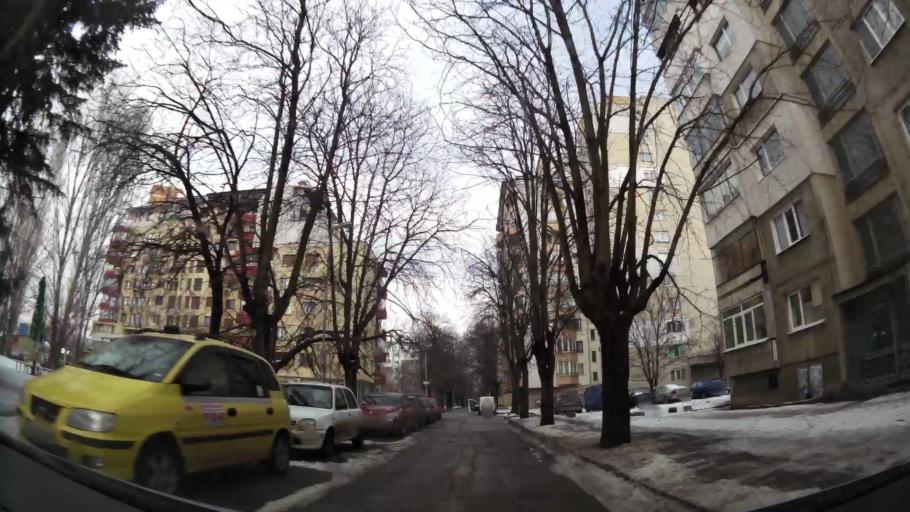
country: BG
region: Sofia-Capital
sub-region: Stolichna Obshtina
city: Sofia
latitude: 42.7100
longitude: 23.2895
